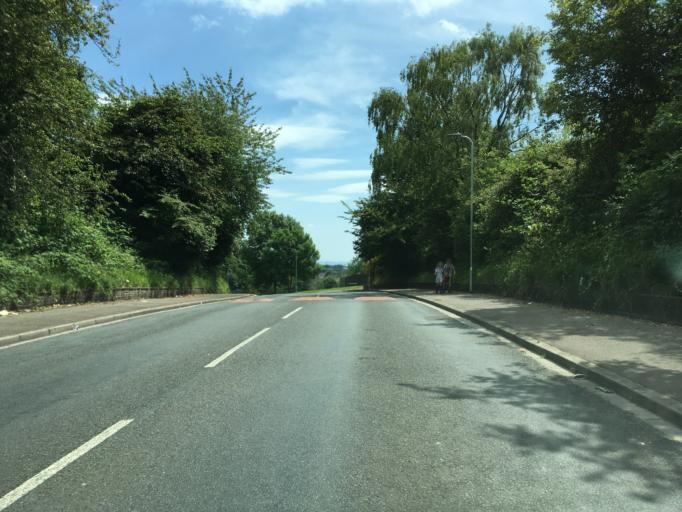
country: GB
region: Wales
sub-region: Newport
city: Caerleon
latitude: 51.5866
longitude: -2.9554
